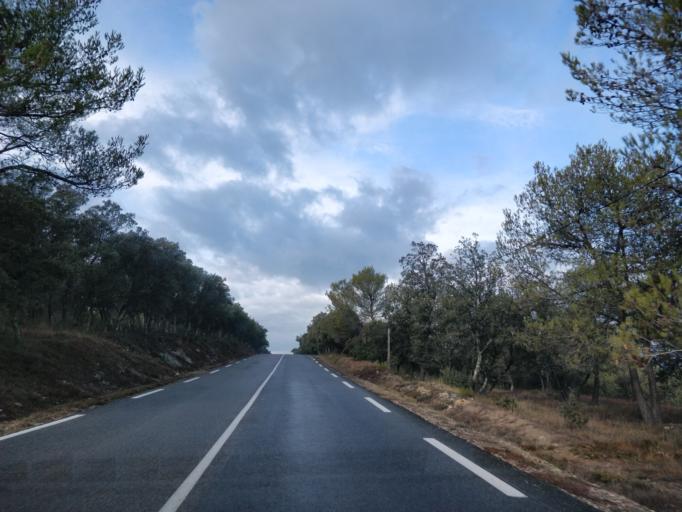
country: FR
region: Languedoc-Roussillon
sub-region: Departement du Gard
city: La Calmette
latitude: 43.8741
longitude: 4.2703
